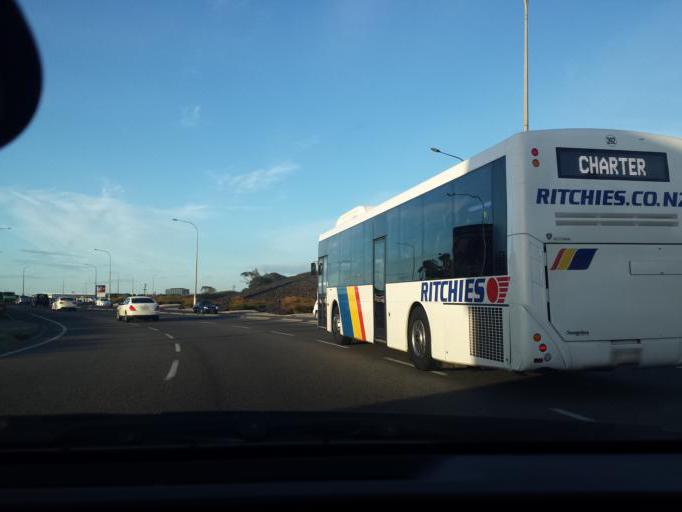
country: NZ
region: Auckland
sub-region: Auckland
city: Mangere
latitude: -36.9913
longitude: 174.7863
